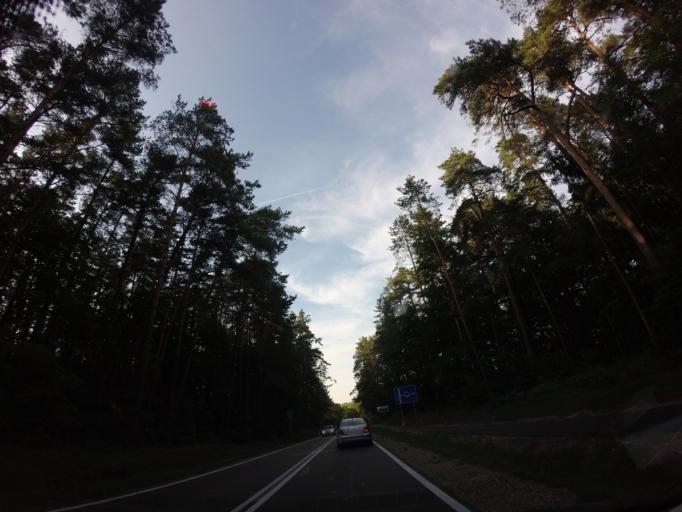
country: PL
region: Podlasie
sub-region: Powiat augustowski
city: Augustow
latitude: 53.8651
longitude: 23.0900
